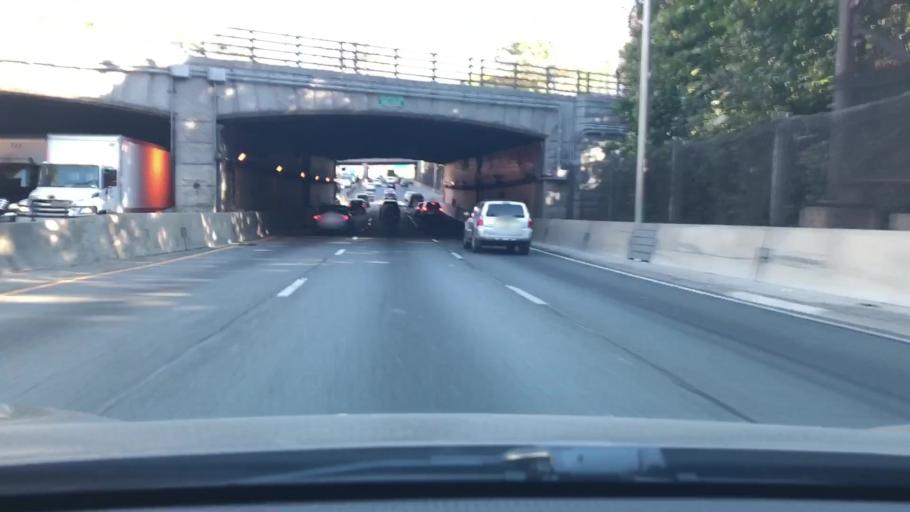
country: US
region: New York
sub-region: Bronx
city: The Bronx
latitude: 40.8406
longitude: -73.8865
